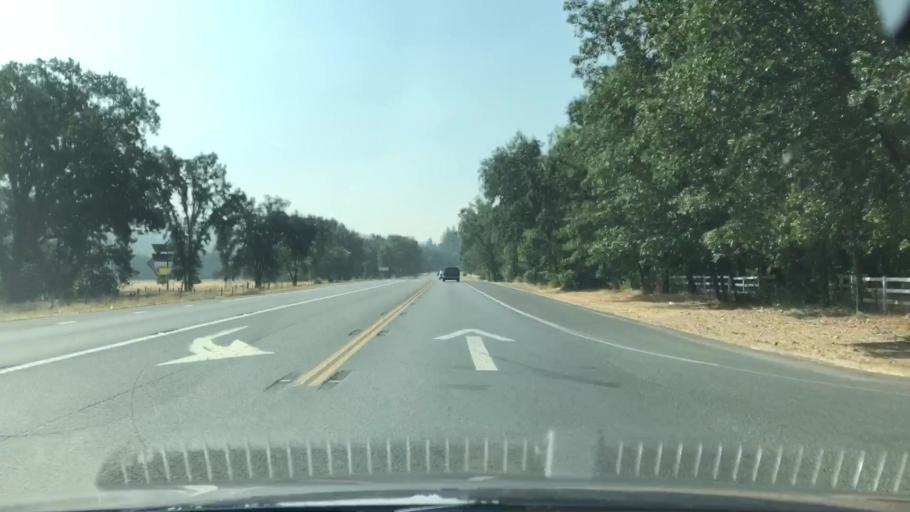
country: US
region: California
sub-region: Lake County
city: Middletown
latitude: 38.7314
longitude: -122.6227
